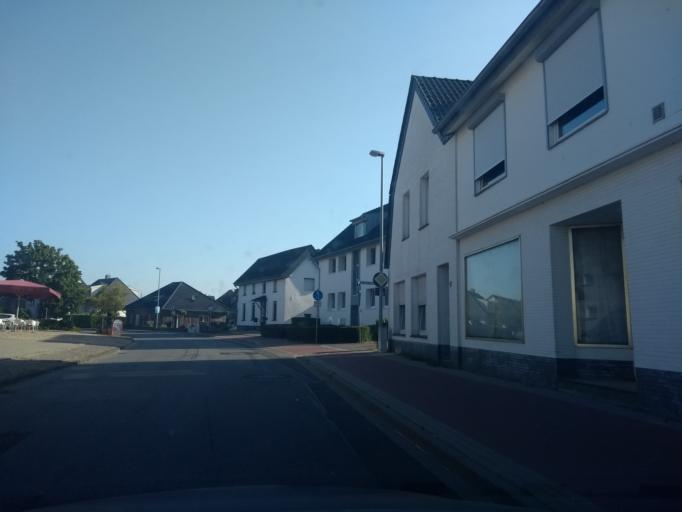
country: DE
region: North Rhine-Westphalia
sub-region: Regierungsbezirk Dusseldorf
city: Kleve
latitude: 51.8119
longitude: 6.1229
